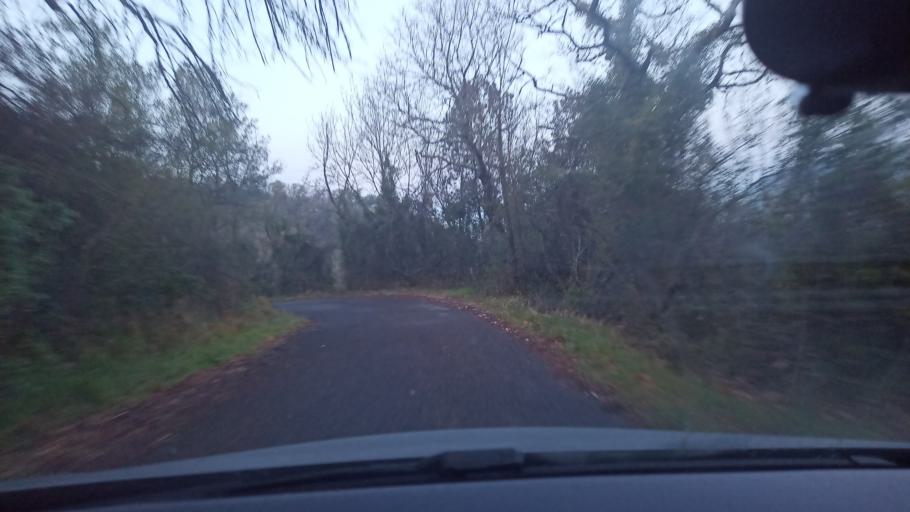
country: IT
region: Latium
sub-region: Provincia di Rieti
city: Cottanello
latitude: 42.4089
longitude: 12.6830
